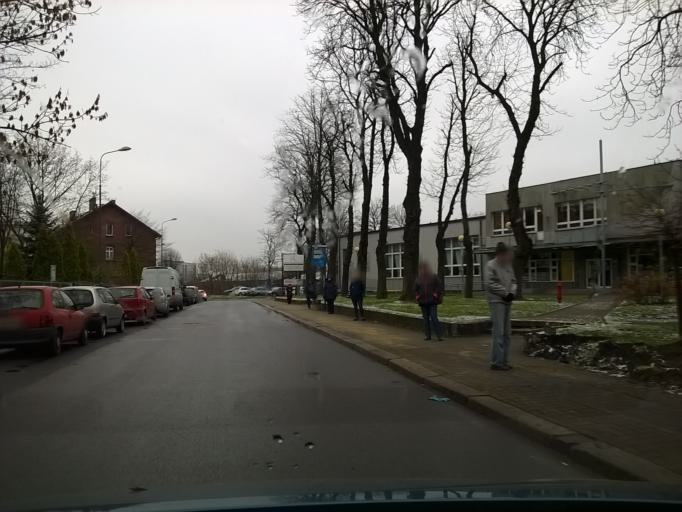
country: PL
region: Silesian Voivodeship
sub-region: Swietochlowice
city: Swietochlowice
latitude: 50.2972
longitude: 18.9427
